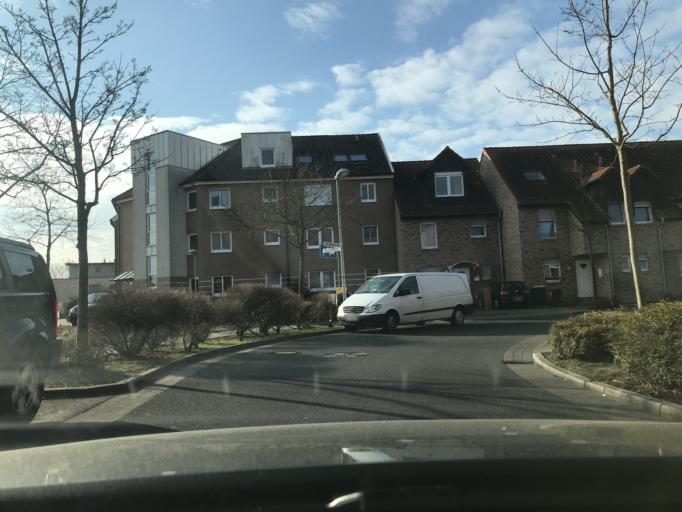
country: DE
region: North Rhine-Westphalia
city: Tonisvorst
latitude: 51.3288
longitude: 6.5277
